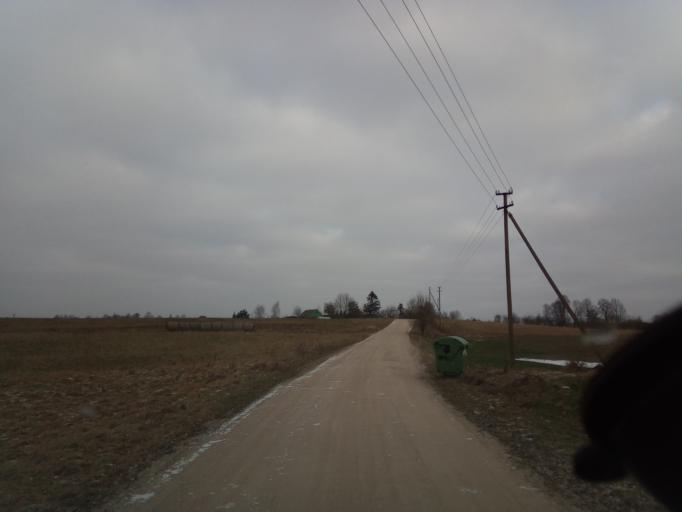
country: LT
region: Alytaus apskritis
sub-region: Alytaus rajonas
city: Daugai
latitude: 54.3692
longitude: 24.4475
